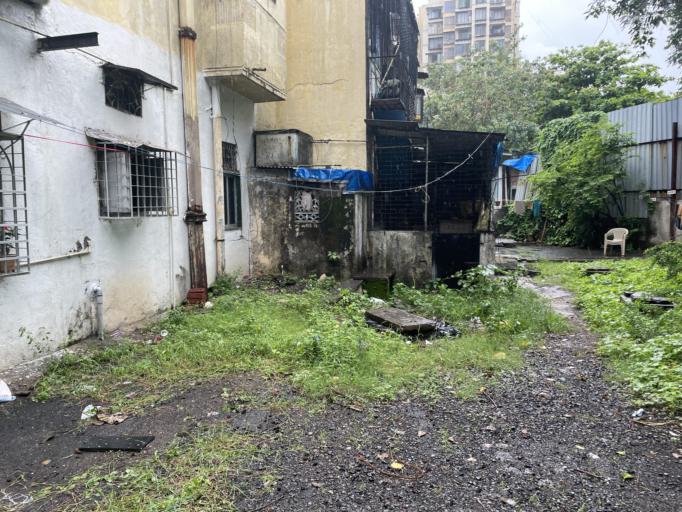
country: IN
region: Maharashtra
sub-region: Mumbai Suburban
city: Borivli
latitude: 19.2339
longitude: 72.8609
